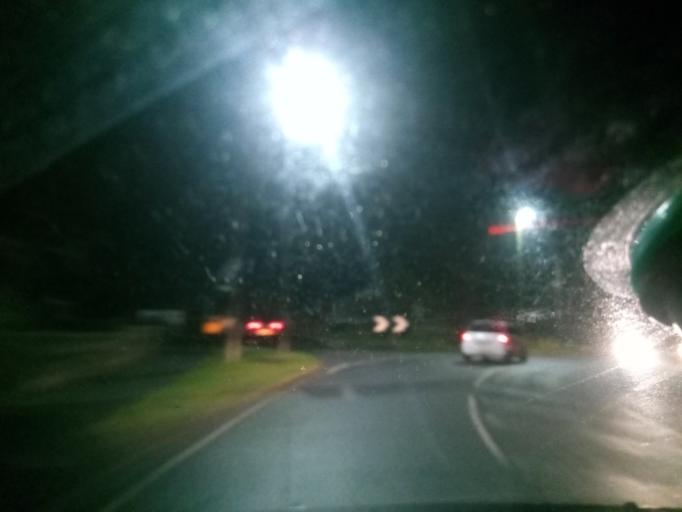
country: GB
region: England
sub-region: Northumberland
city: Meldon
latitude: 55.1018
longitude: -1.8409
